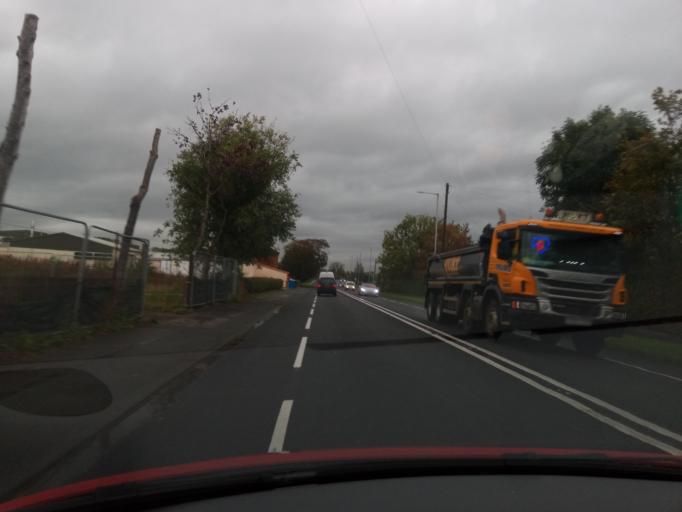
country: GB
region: England
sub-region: Lancashire
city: Catterall
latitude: 53.8348
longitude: -2.7387
